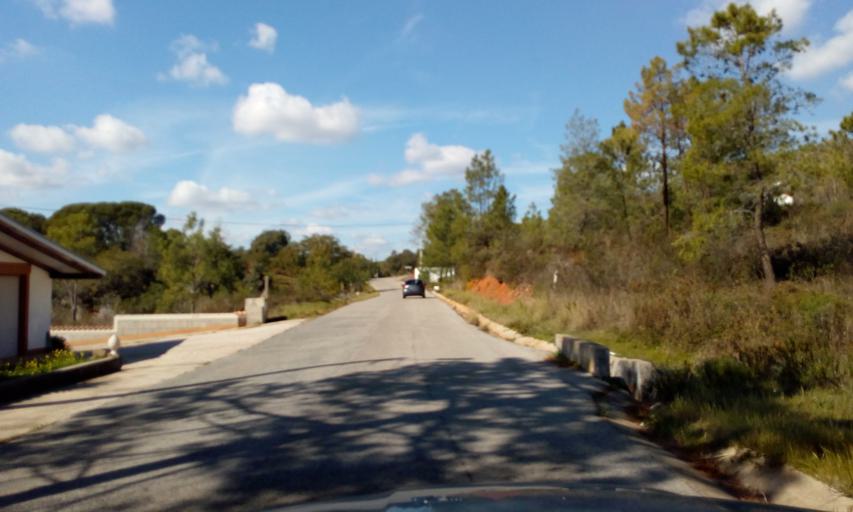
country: PT
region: Faro
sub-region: Loule
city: Loule
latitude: 37.2463
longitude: -8.0799
